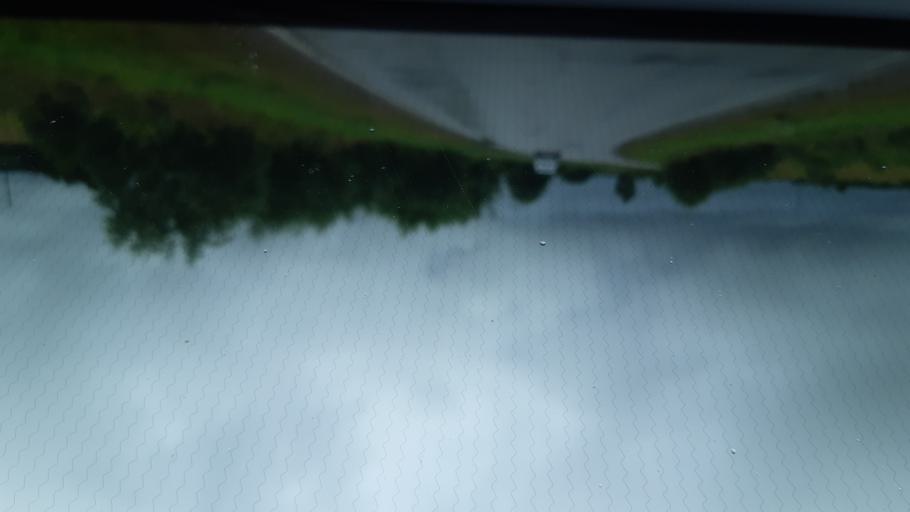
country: RU
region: Smolensk
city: Gagarin
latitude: 55.6177
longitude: 34.9657
